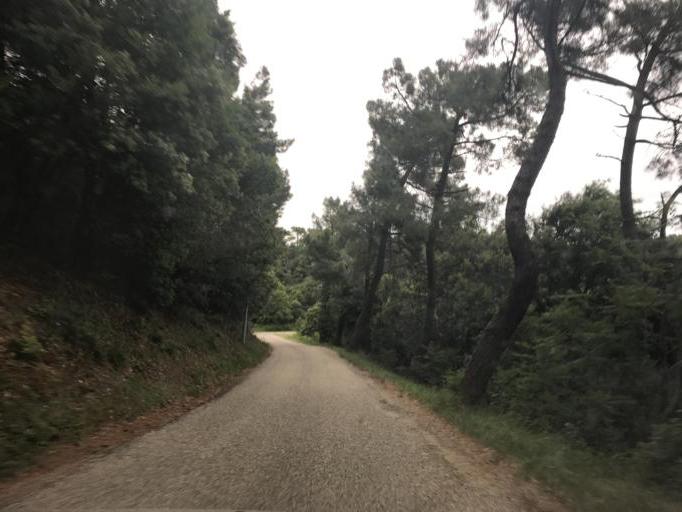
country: FR
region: Rhone-Alpes
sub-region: Departement de l'Ardeche
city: La Voulte-sur-Rhone
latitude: 44.8043
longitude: 4.7481
